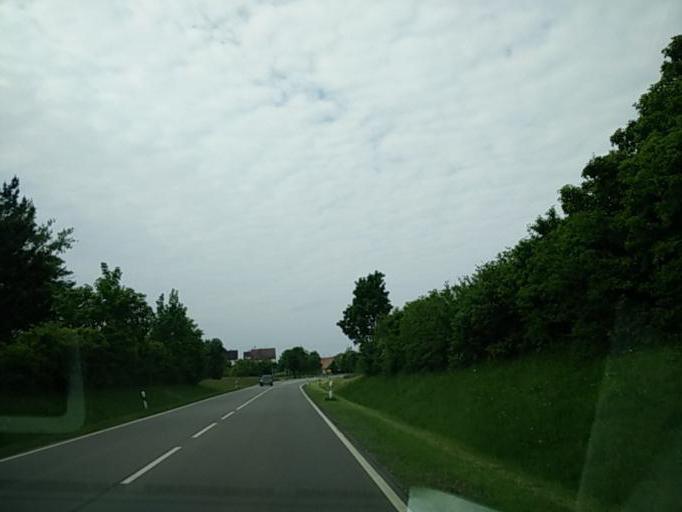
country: DE
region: Baden-Wuerttemberg
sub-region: Tuebingen Region
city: Rottenburg
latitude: 48.4523
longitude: 8.9210
